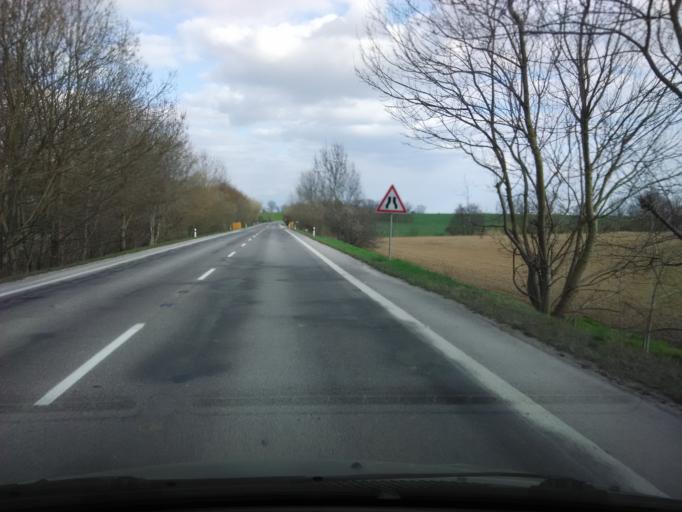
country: SK
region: Nitriansky
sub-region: Okres Nitra
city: Vrable
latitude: 48.3625
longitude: 18.2732
